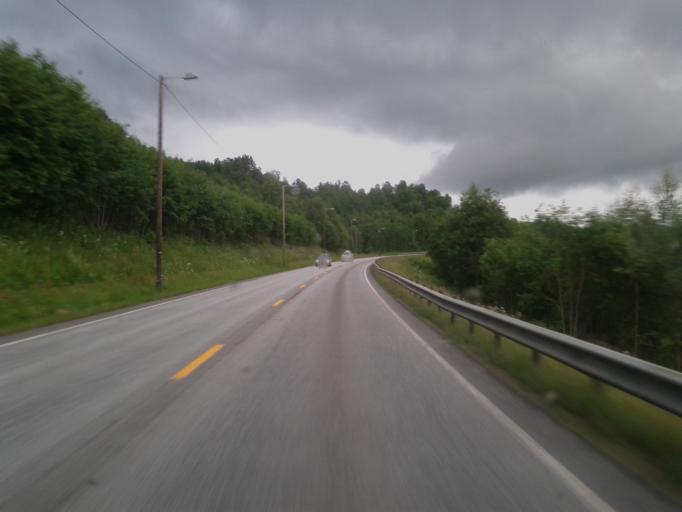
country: NO
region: Sor-Trondelag
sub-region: Melhus
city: Lundamo
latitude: 63.1158
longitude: 10.2424
